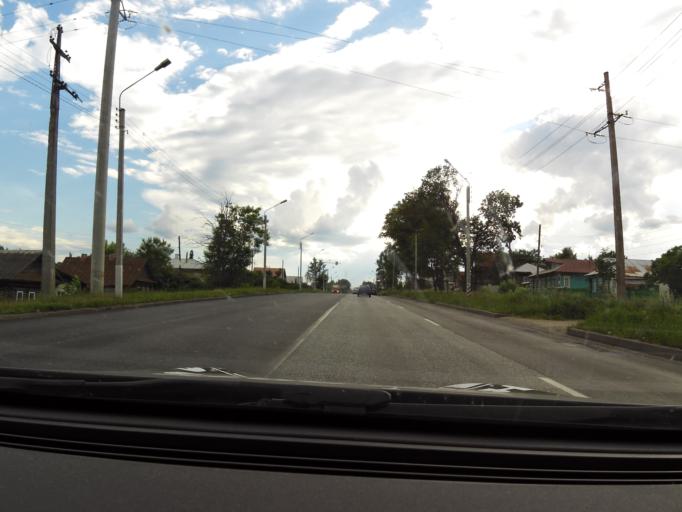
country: RU
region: Vladimir
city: Gorokhovets
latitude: 56.1943
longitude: 42.6914
